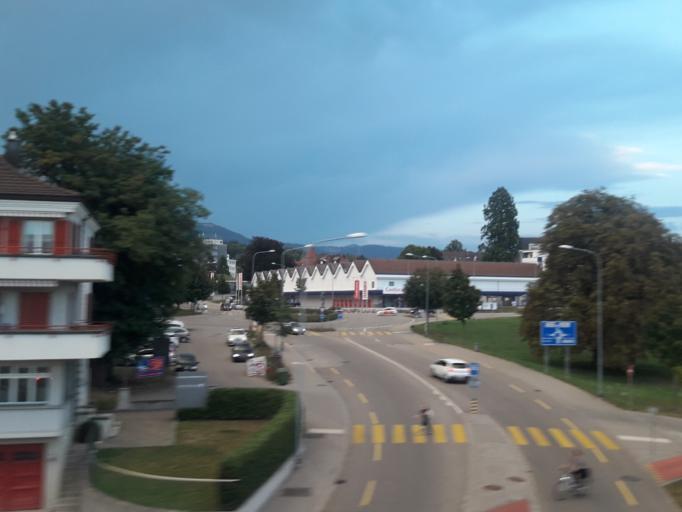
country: CH
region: Solothurn
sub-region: Bezirk Solothurn
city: Solothurn
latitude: 47.2101
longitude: 7.5252
